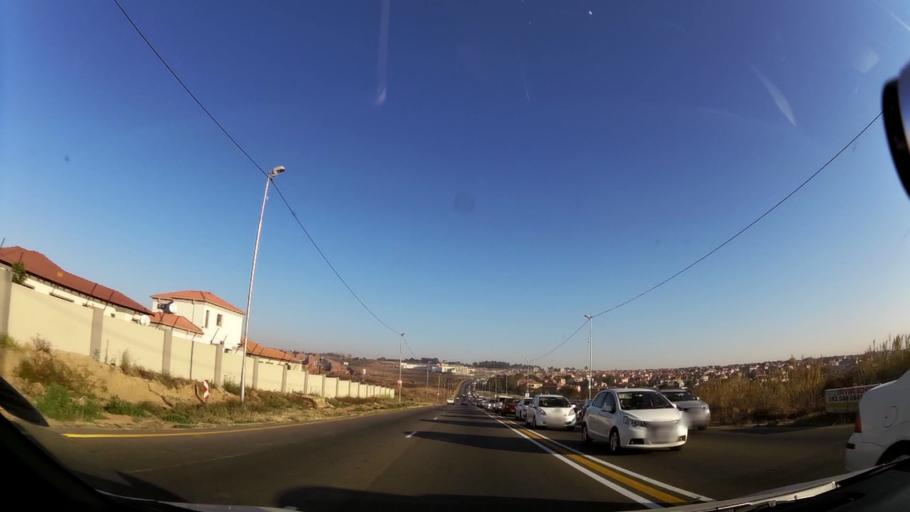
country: ZA
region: Gauteng
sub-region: City of Johannesburg Metropolitan Municipality
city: Midrand
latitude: -25.9477
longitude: 28.1154
